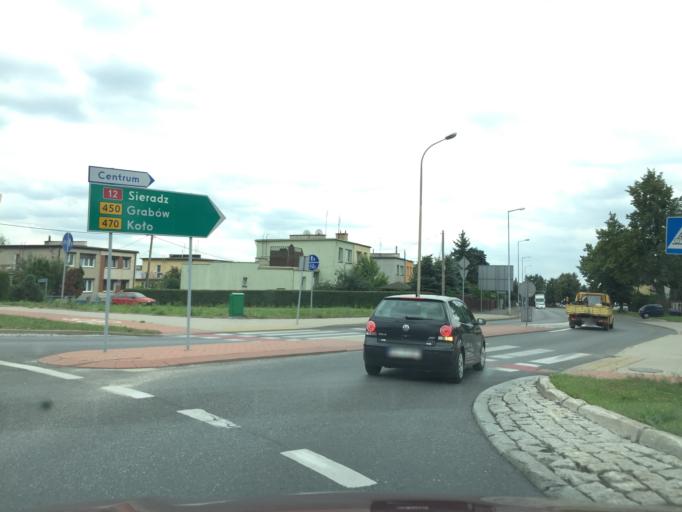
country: PL
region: Greater Poland Voivodeship
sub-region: Kalisz
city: Kalisz
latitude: 51.7783
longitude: 18.0890
